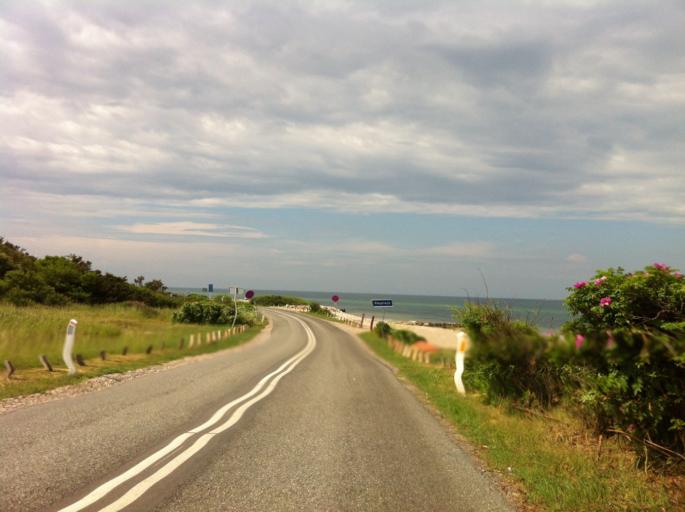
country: DK
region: Capital Region
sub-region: Gribskov Kommune
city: Helsinge
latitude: 56.1069
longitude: 12.1787
